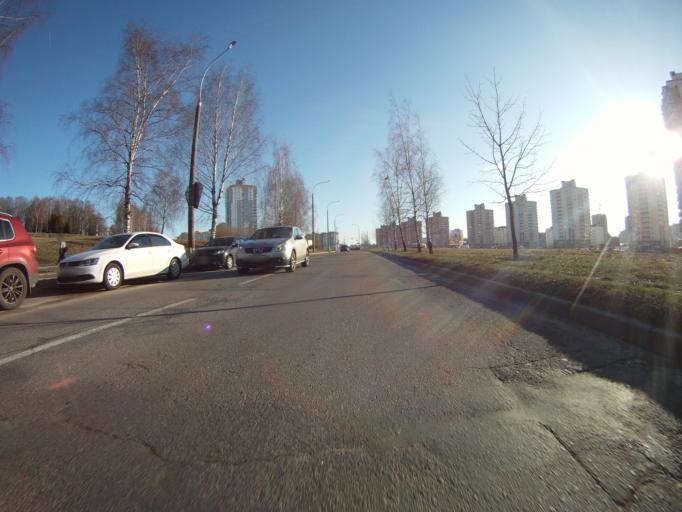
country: BY
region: Minsk
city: Novoye Medvezhino
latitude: 53.8788
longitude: 27.4468
